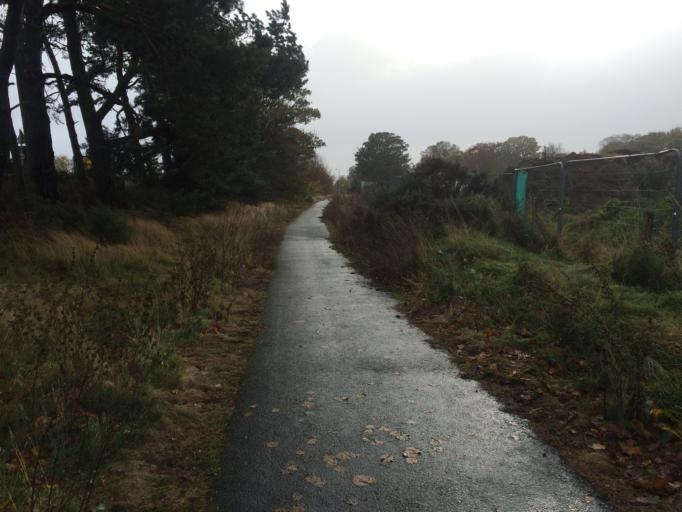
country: GB
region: Scotland
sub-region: Highland
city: Alness
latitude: 57.6923
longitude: -4.2438
